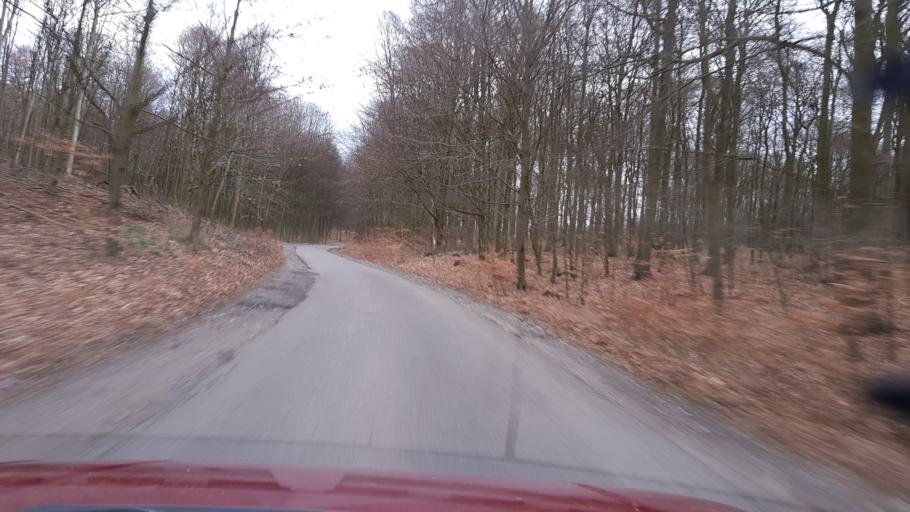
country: PL
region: West Pomeranian Voivodeship
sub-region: Szczecin
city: Szczecin
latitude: 53.3477
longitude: 14.6110
